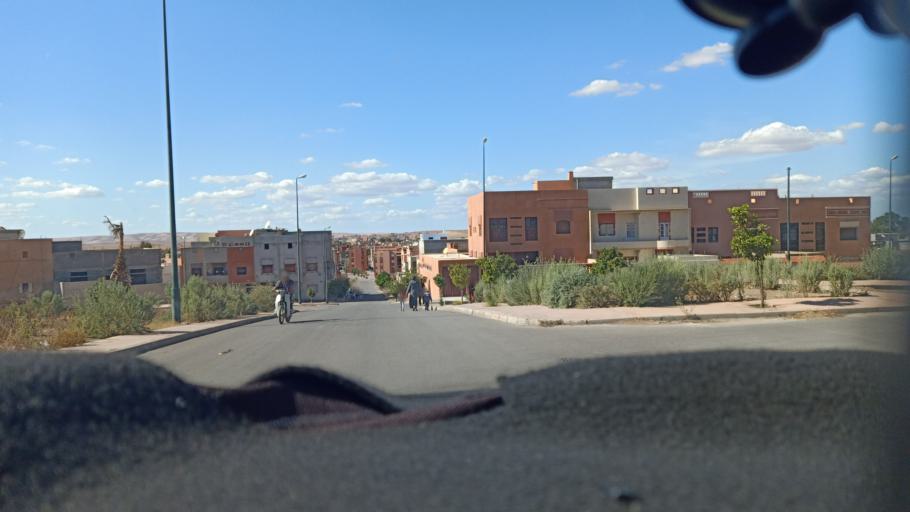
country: MA
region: Doukkala-Abda
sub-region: Safi
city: Youssoufia
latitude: 32.2389
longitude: -8.5318
